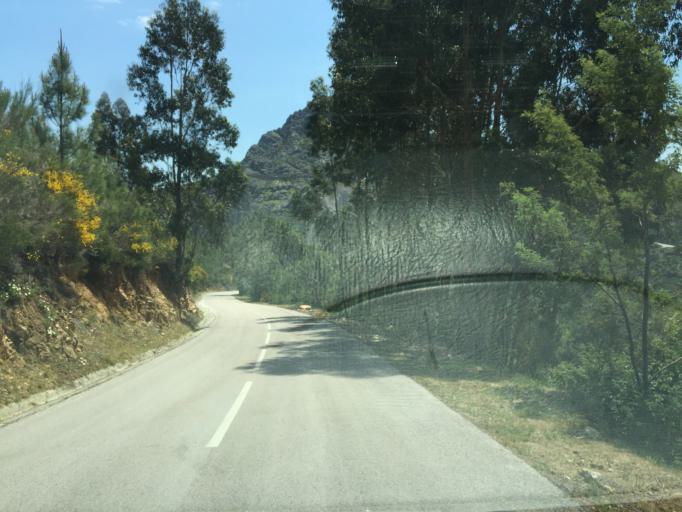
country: PT
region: Coimbra
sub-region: Pampilhosa da Serra
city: Pampilhosa da Serra
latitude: 40.0919
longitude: -7.8675
